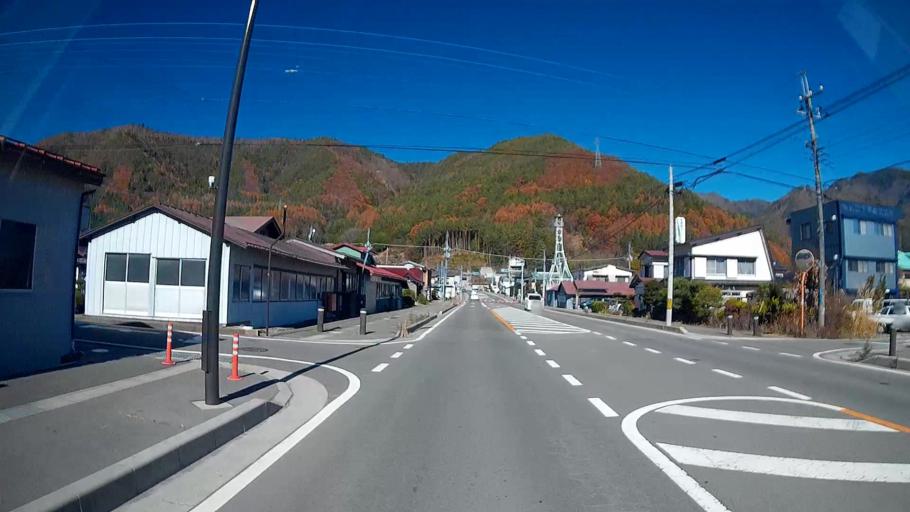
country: JP
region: Yamanashi
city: Fujikawaguchiko
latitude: 35.4969
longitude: 138.7920
